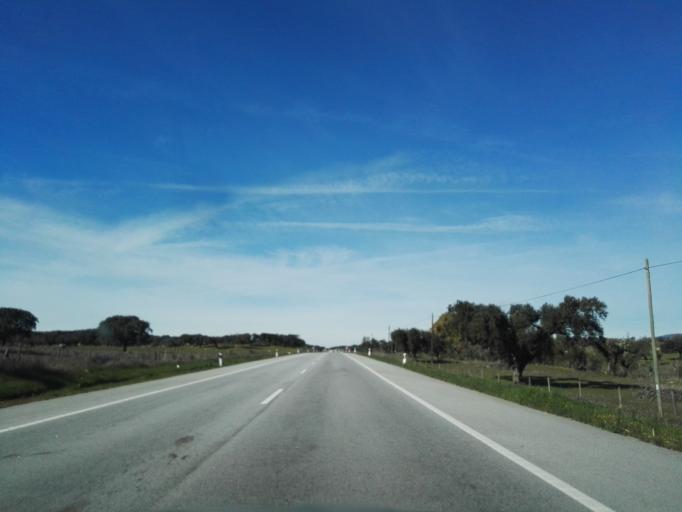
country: PT
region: Portalegre
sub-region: Arronches
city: Arronches
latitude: 39.1653
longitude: -7.3265
